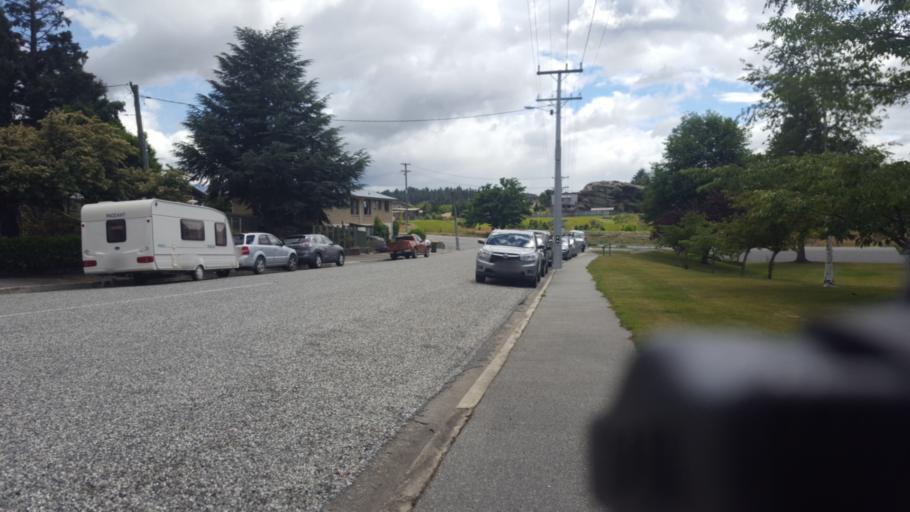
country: NZ
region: Otago
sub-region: Queenstown-Lakes District
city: Wanaka
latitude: -45.2559
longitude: 169.3945
